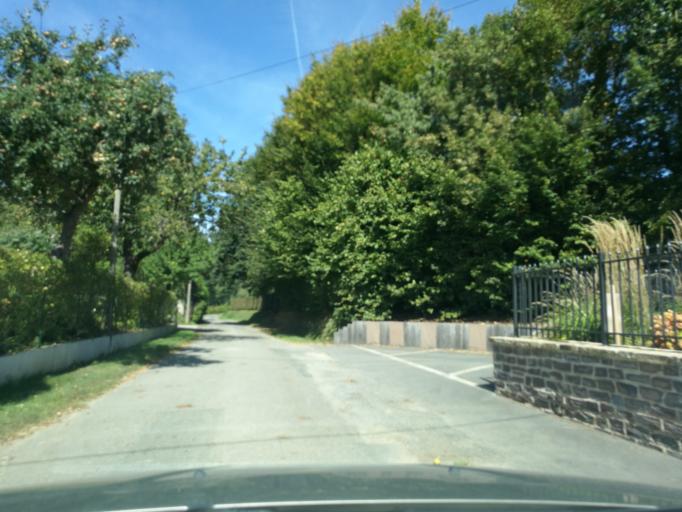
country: FR
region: Brittany
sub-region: Departement d'Ille-et-Vilaine
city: Bedee
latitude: 48.1677
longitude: -1.9485
